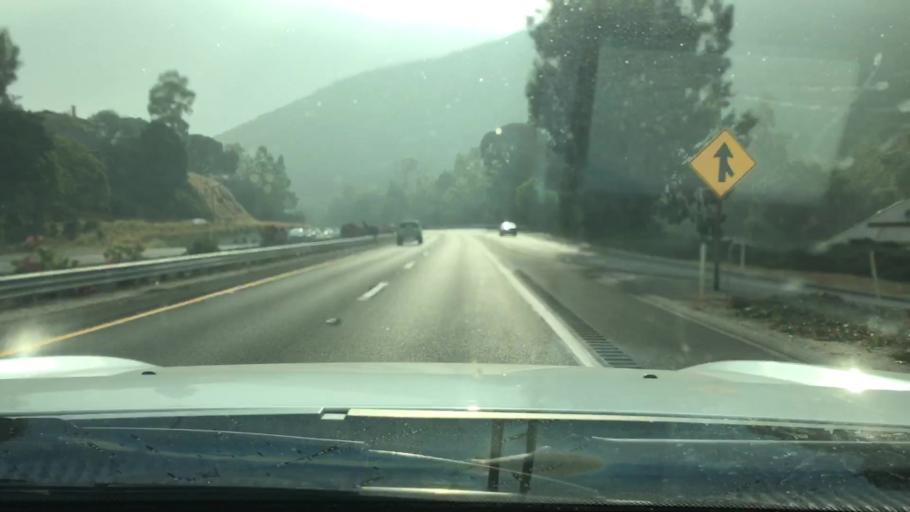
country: US
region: California
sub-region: San Luis Obispo County
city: San Luis Obispo
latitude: 35.2917
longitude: -120.6536
